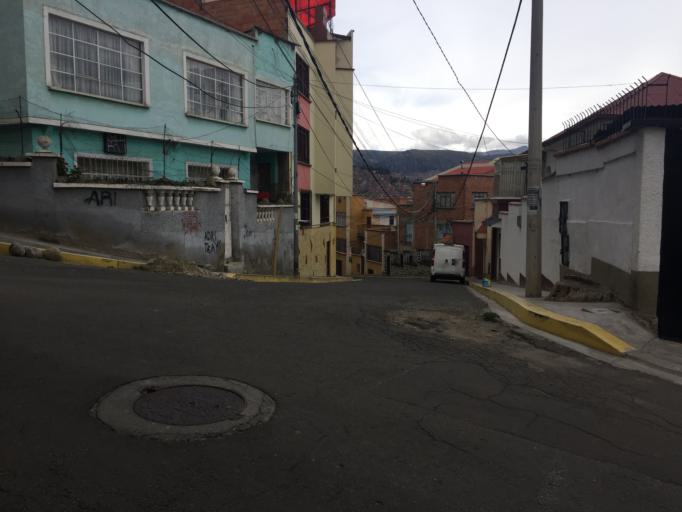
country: BO
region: La Paz
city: La Paz
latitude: -16.5119
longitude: -68.1347
